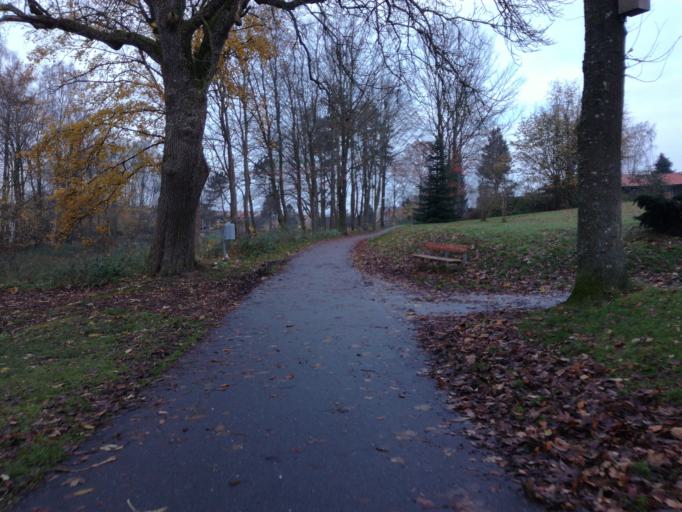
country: DK
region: South Denmark
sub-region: Vejle Kommune
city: Borkop
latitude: 55.6370
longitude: 9.6458
